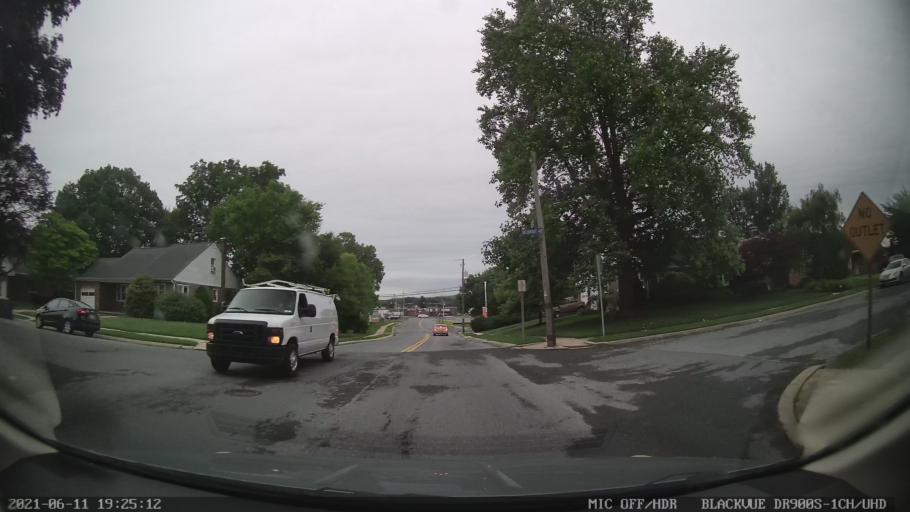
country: US
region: Pennsylvania
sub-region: Berks County
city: Sinking Spring
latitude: 40.3272
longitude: -76.0088
